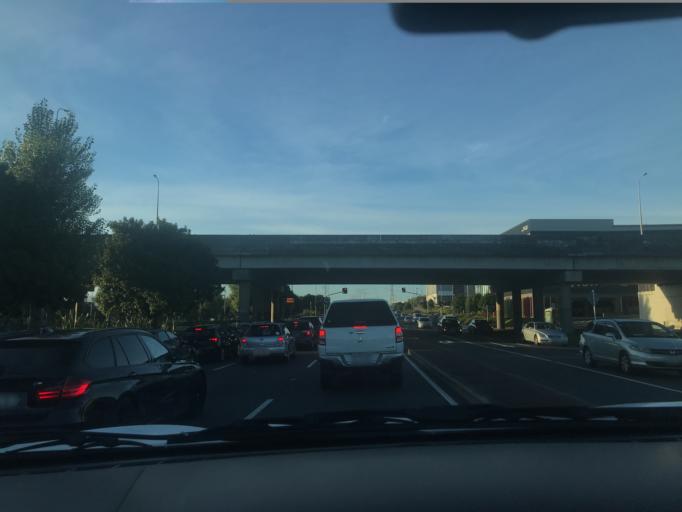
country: NZ
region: Auckland
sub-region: Auckland
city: Tamaki
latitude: -36.9151
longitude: 174.8390
